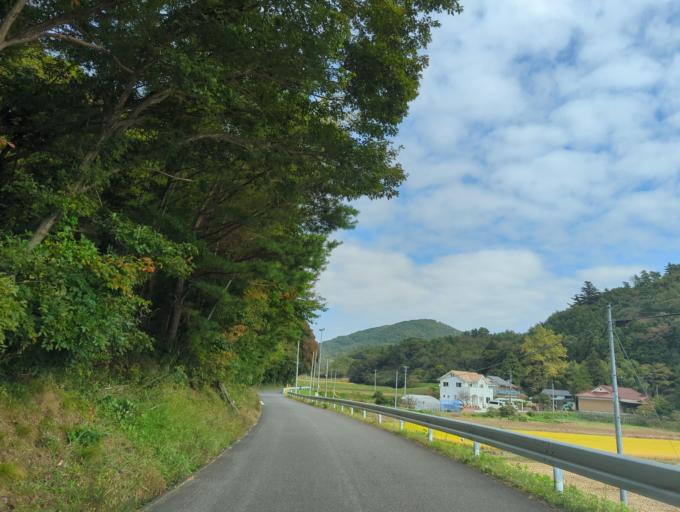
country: JP
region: Fukushima
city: Motomiya
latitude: 37.5135
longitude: 140.3275
